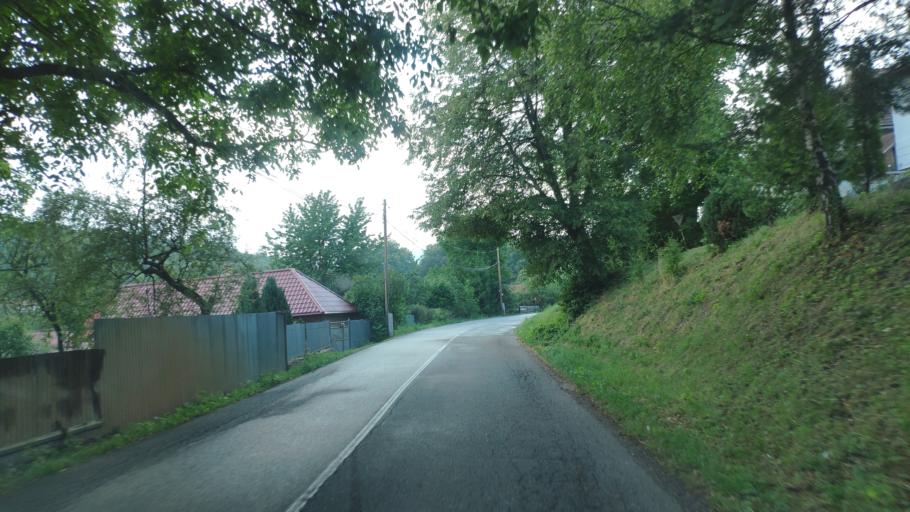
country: SK
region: Kosicky
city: Moldava nad Bodvou
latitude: 48.6861
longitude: 20.9750
